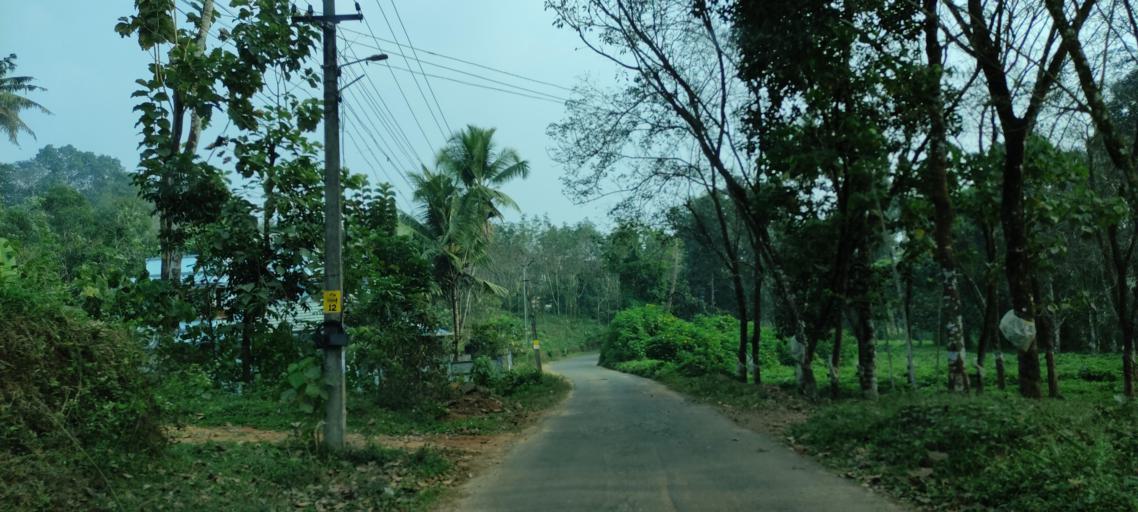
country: IN
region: Kerala
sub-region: Ernakulam
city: Piravam
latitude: 9.8162
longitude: 76.5291
